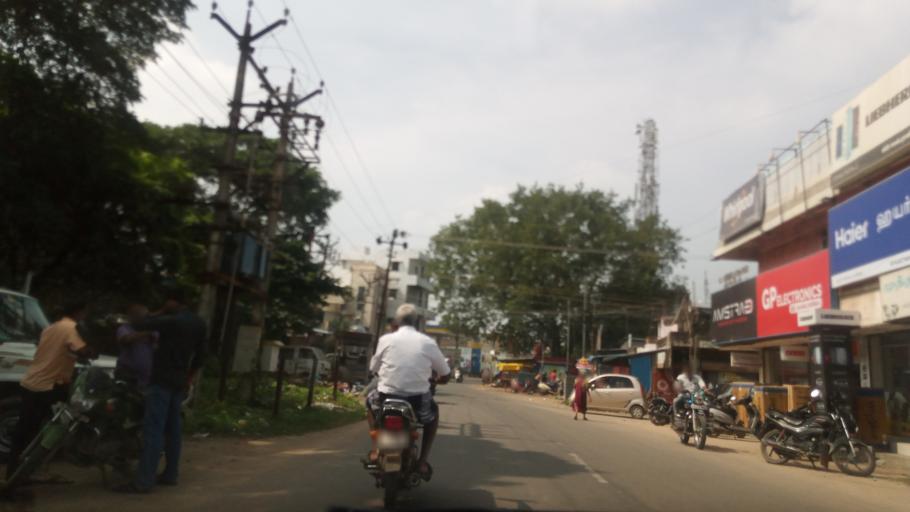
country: IN
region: Tamil Nadu
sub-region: Vellore
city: Arakkonam
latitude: 13.0840
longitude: 79.6644
